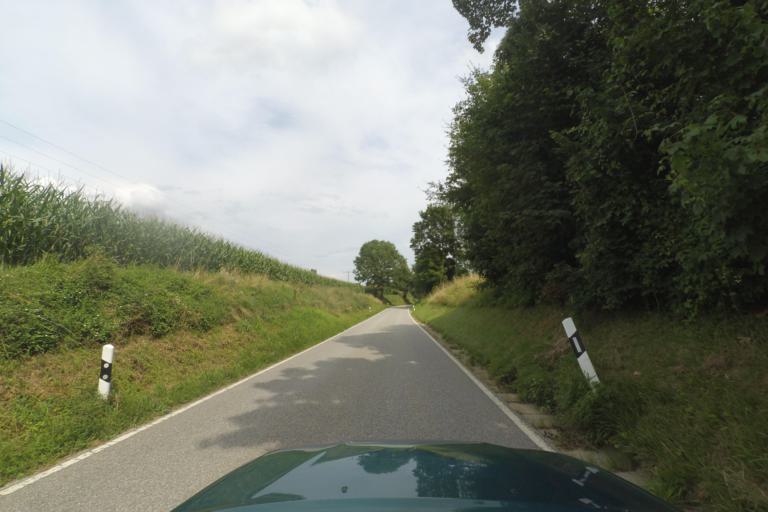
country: DE
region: Bavaria
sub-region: Lower Bavaria
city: Landau an der Isar
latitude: 48.6819
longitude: 12.7405
